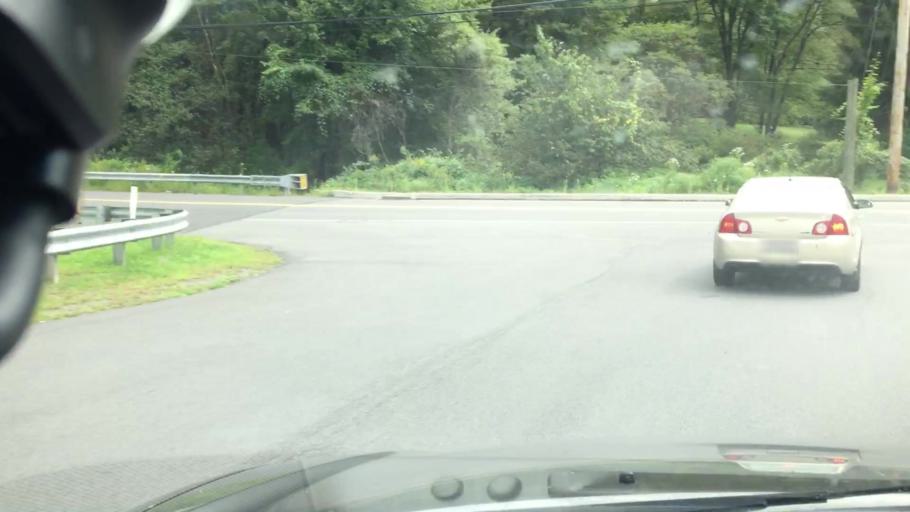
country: US
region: Pennsylvania
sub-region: Luzerne County
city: Nanticoke
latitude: 41.1914
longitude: -75.9886
